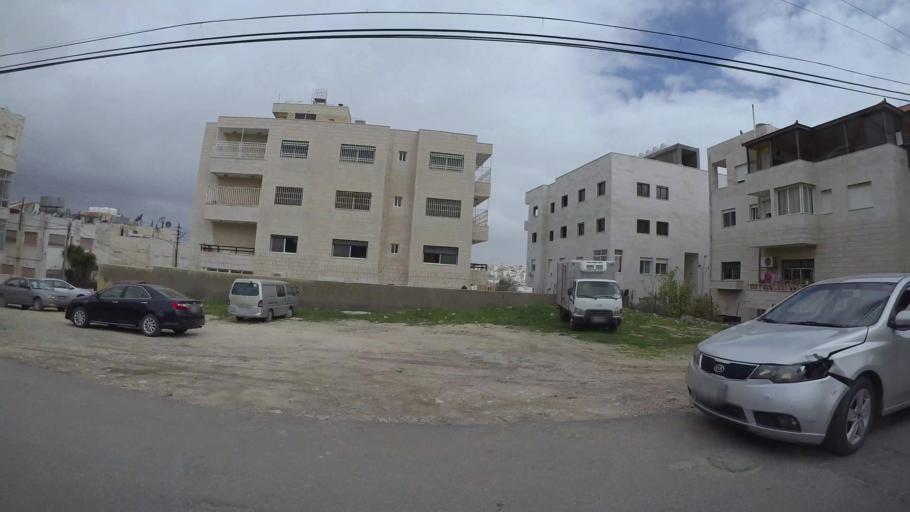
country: JO
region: Amman
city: Wadi as Sir
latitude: 31.9533
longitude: 35.8303
